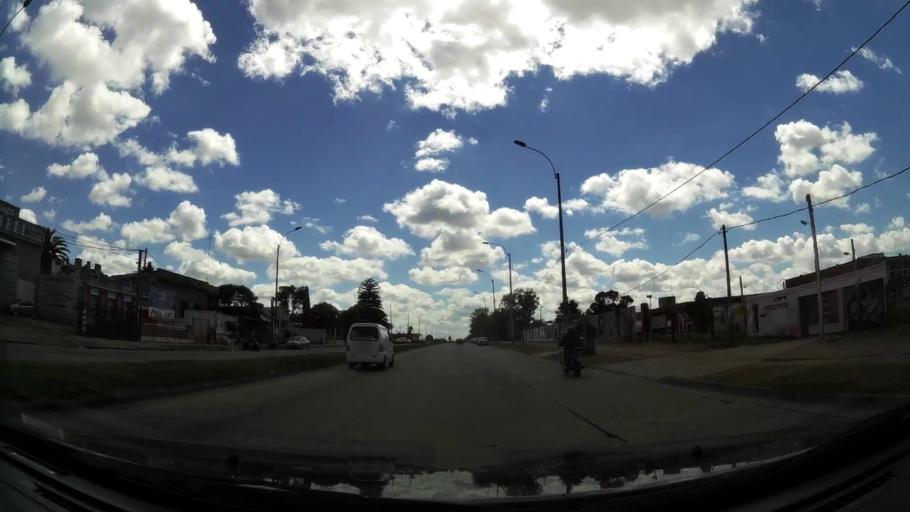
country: UY
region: Canelones
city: Paso de Carrasco
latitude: -34.8390
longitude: -56.1200
